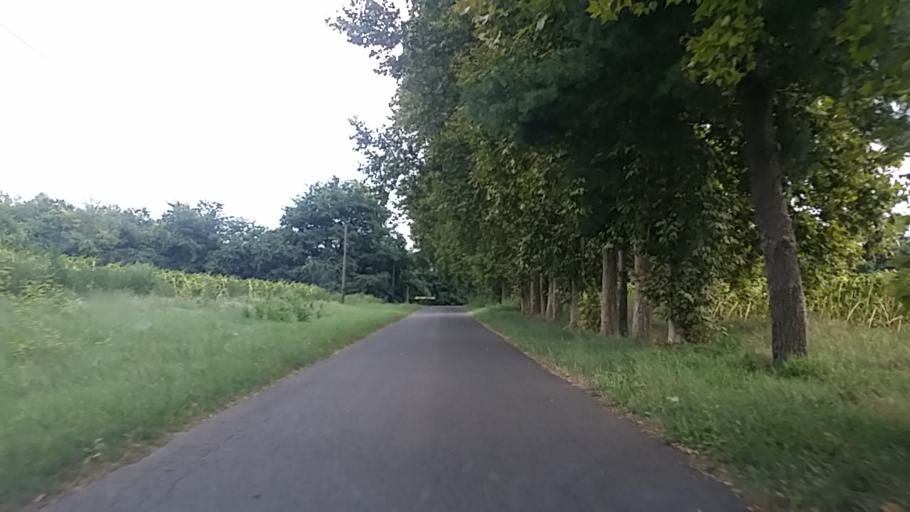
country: HU
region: Tolna
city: Szedres
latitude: 46.5265
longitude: 18.6392
